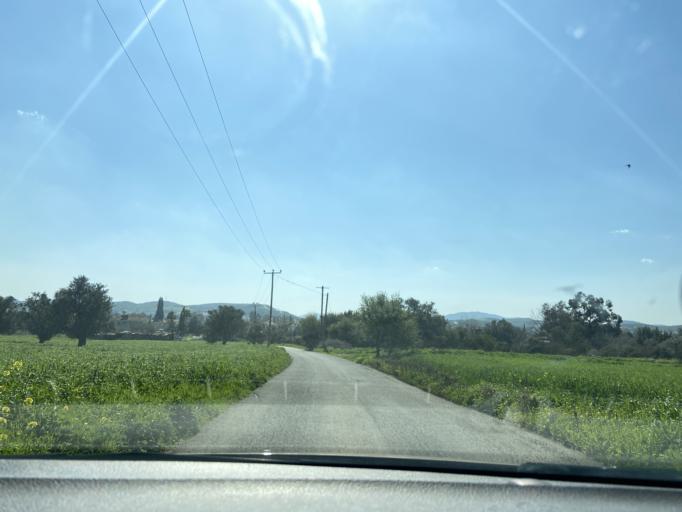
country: CY
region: Lefkosia
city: Dali
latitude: 35.0269
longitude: 33.3908
